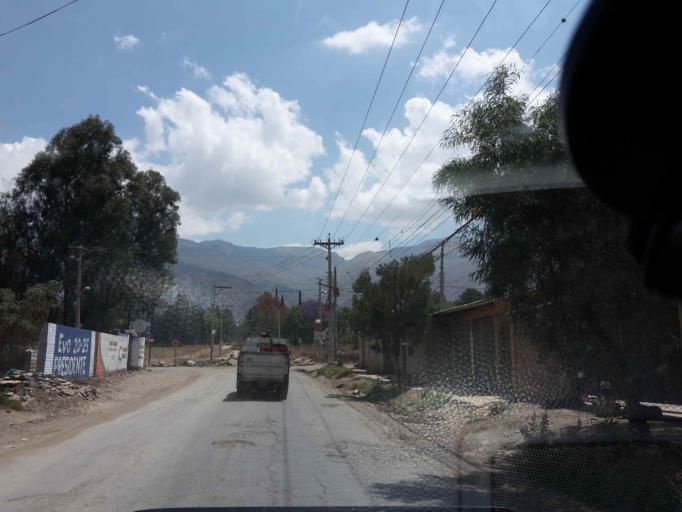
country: BO
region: Cochabamba
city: Cochabamba
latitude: -17.3494
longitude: -66.2250
